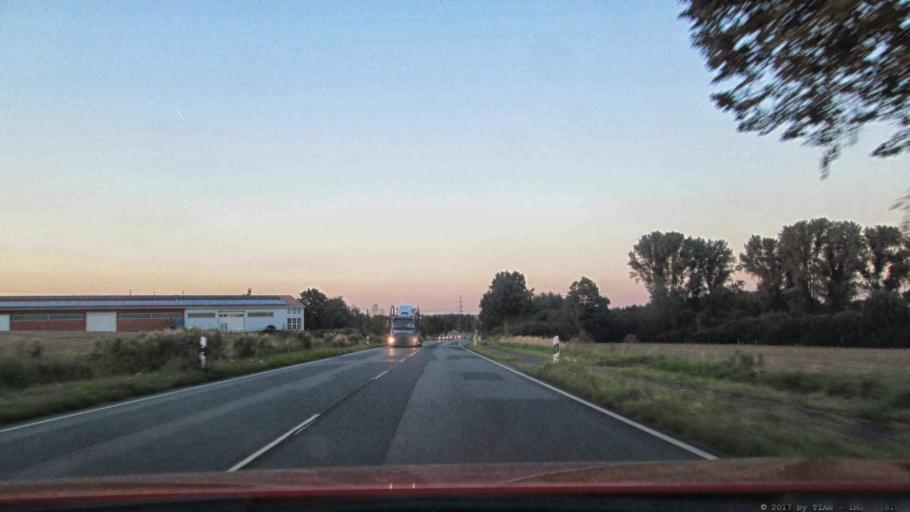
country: DE
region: Lower Saxony
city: Lehre
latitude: 52.3515
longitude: 10.6925
